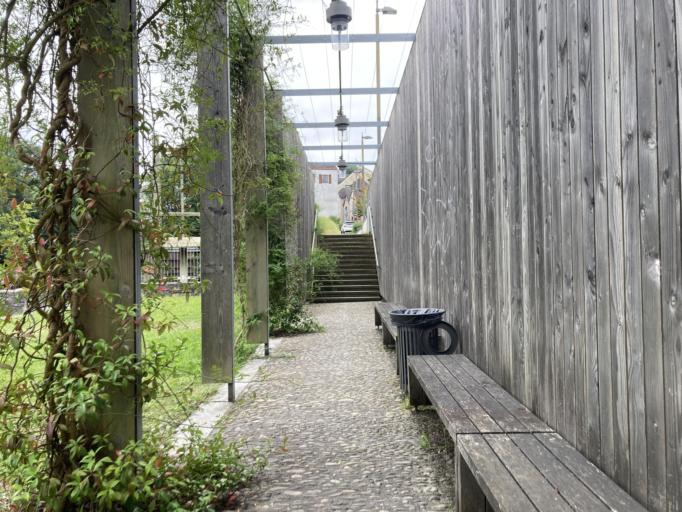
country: FR
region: Aquitaine
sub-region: Departement des Pyrenees-Atlantiques
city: Oloron-Sainte-Marie
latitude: 43.1939
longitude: -0.6077
